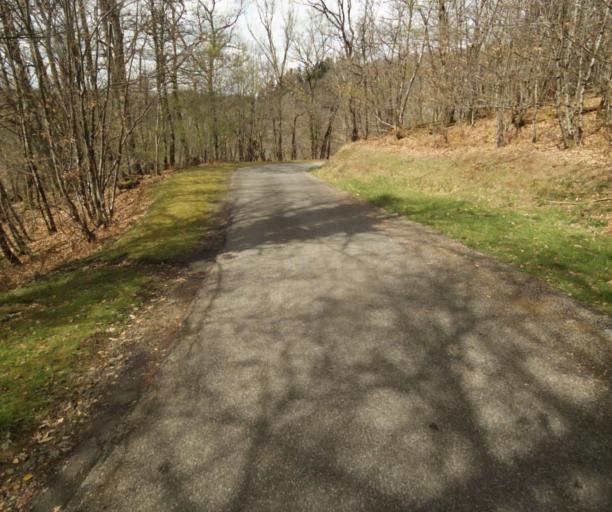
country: FR
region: Limousin
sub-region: Departement de la Correze
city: Sainte-Fortunade
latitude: 45.1952
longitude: 1.8785
